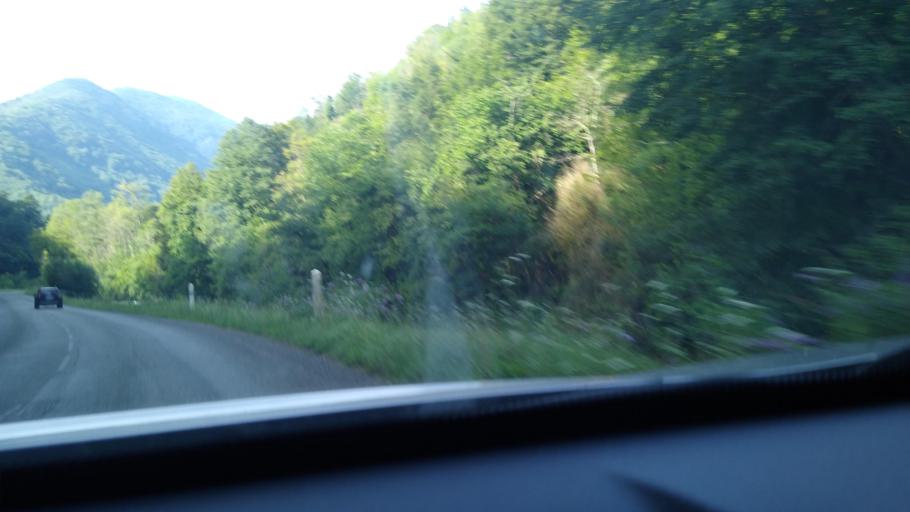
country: FR
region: Midi-Pyrenees
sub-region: Departement de l'Ariege
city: Saint-Girons
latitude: 42.8526
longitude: 1.1931
